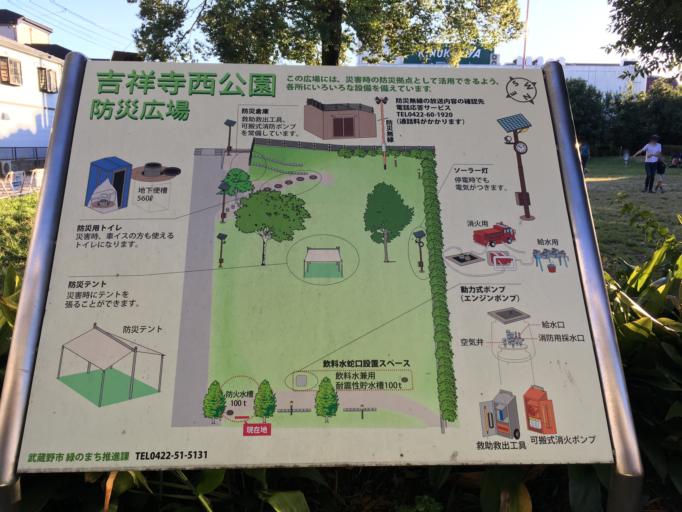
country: JP
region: Tokyo
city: Musashino
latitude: 35.7052
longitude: 139.5727
